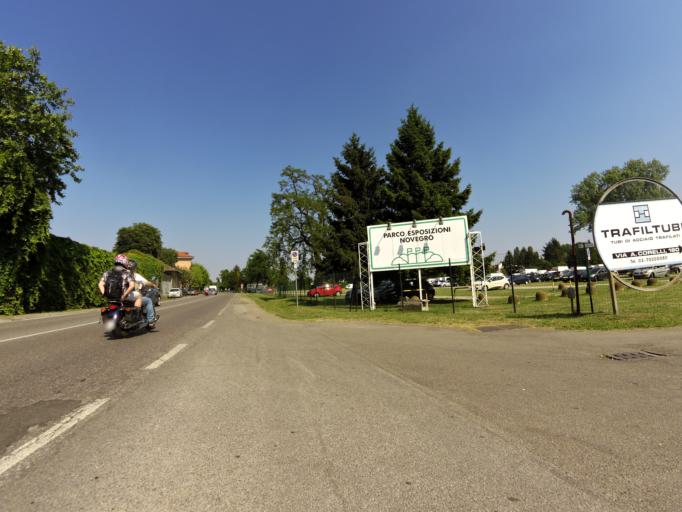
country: IT
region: Lombardy
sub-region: Citta metropolitana di Milano
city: Novegro-Tregarezzo-San Felice
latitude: 45.4726
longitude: 9.2751
